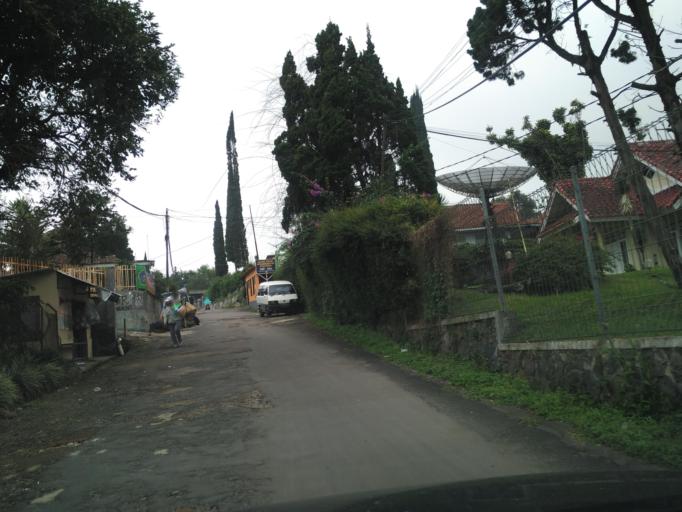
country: ID
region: West Java
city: Sukabumi
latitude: -6.7391
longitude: 107.0415
